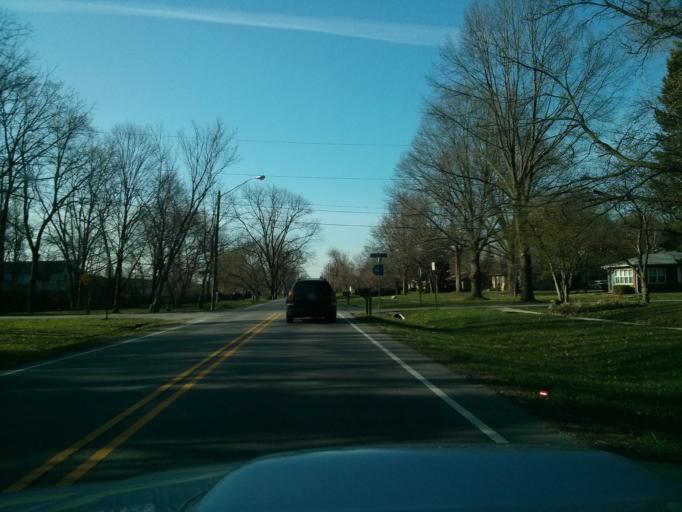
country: US
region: Indiana
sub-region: Marion County
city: Meridian Hills
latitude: 39.9257
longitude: -86.1459
